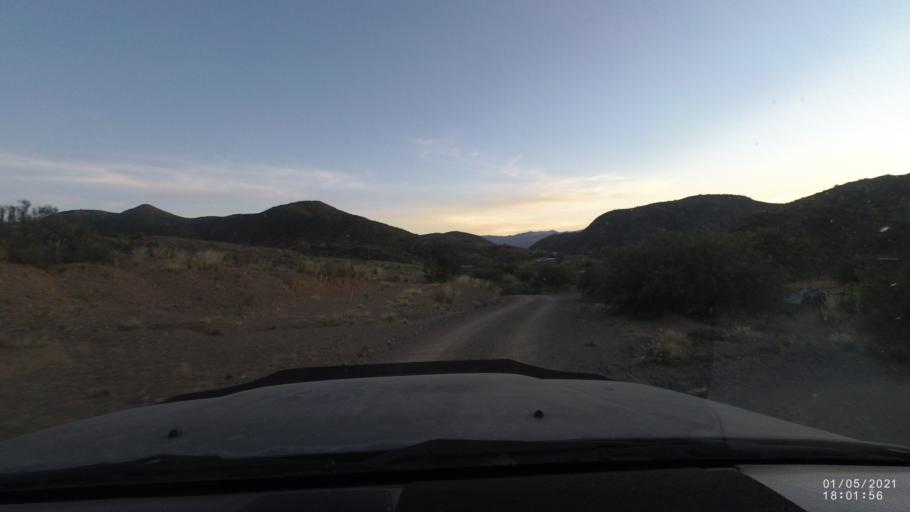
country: BO
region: Cochabamba
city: Capinota
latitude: -17.6862
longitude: -66.1724
